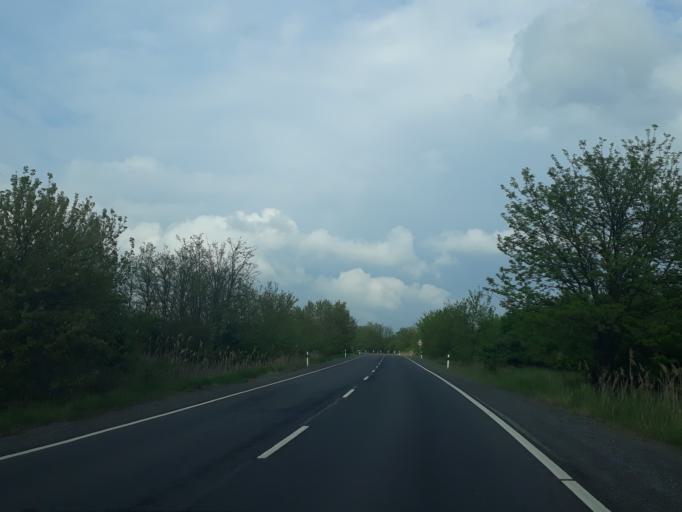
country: HU
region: Szabolcs-Szatmar-Bereg
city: Nyirtass
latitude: 48.1203
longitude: 22.0033
